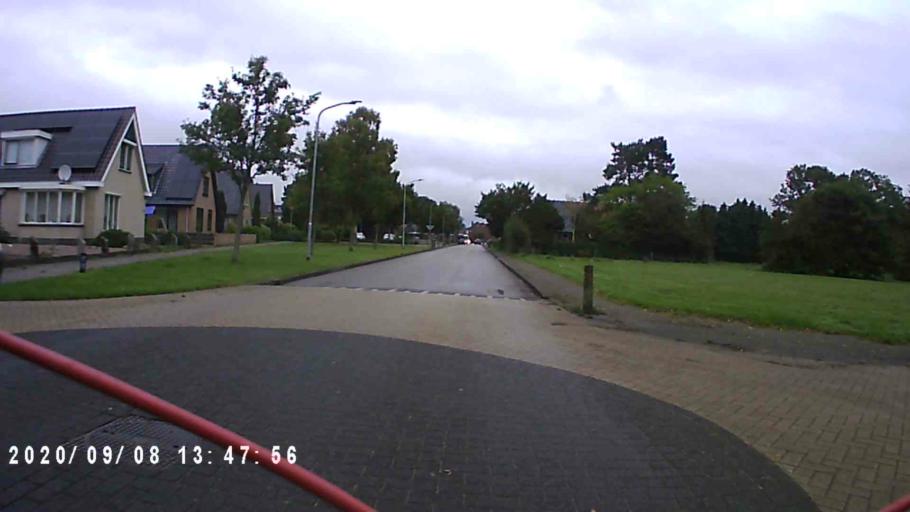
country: NL
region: Groningen
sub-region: Gemeente Veendam
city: Veendam
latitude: 53.1305
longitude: 6.8674
